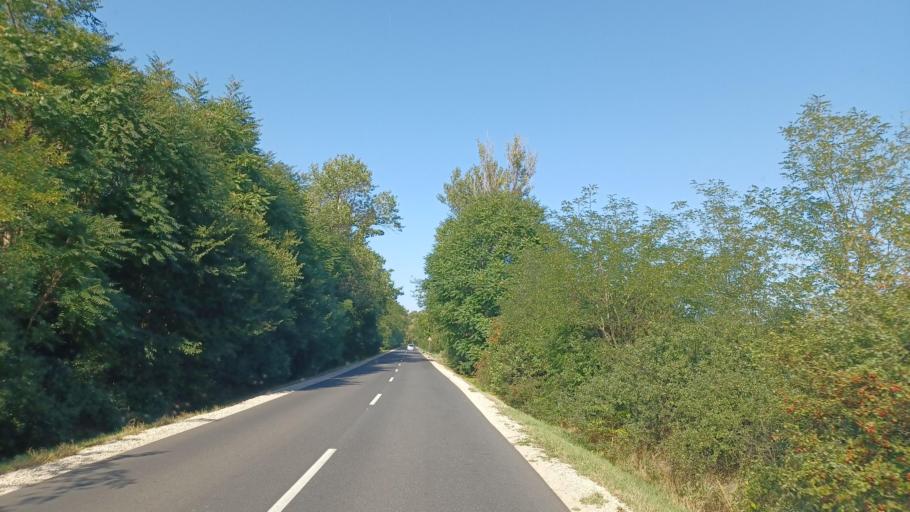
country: HU
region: Fejer
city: Alap
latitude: 46.7461
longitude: 18.6910
